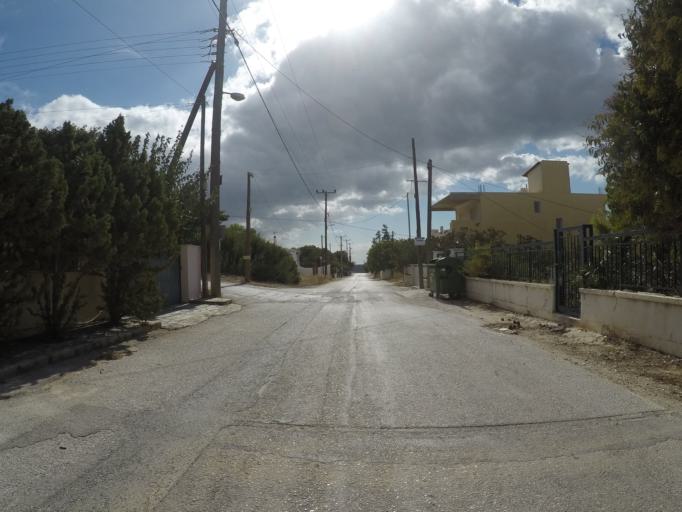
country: GR
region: Attica
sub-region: Nomarchia Anatolikis Attikis
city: Agia Marina
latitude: 37.8166
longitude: 23.8468
